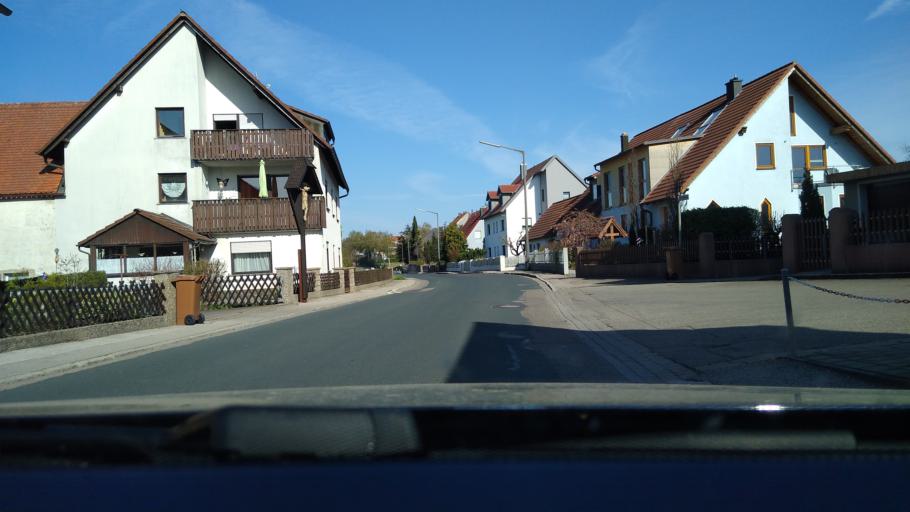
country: DE
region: Bavaria
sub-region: Regierungsbezirk Mittelfranken
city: Mitteleschenbach
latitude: 49.2136
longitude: 10.8023
